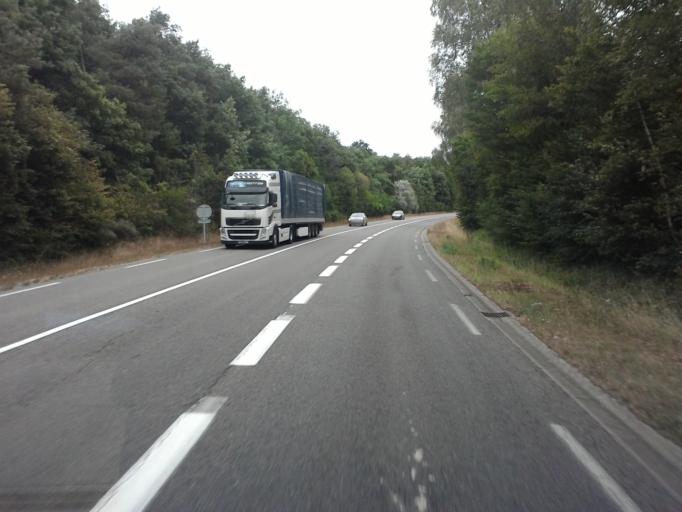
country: FR
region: Lorraine
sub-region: Departement de Meurthe-et-Moselle
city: Colombey-les-Belles
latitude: 48.5756
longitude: 5.9762
